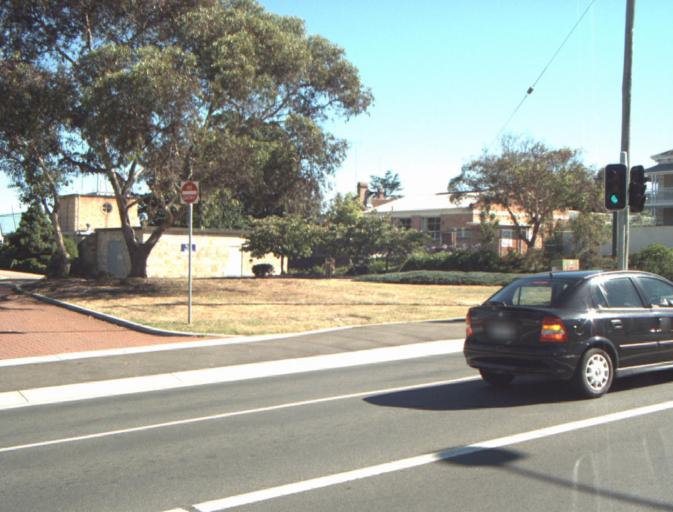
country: AU
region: Tasmania
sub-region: Launceston
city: Launceston
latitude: -41.4400
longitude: 147.1314
